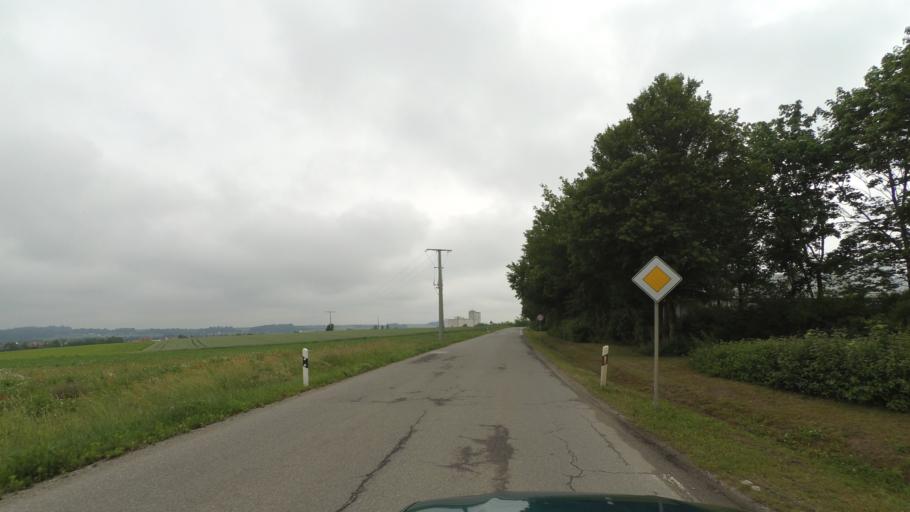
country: DE
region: Bavaria
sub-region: Lower Bavaria
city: Geiselhoring
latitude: 48.8153
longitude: 12.3895
